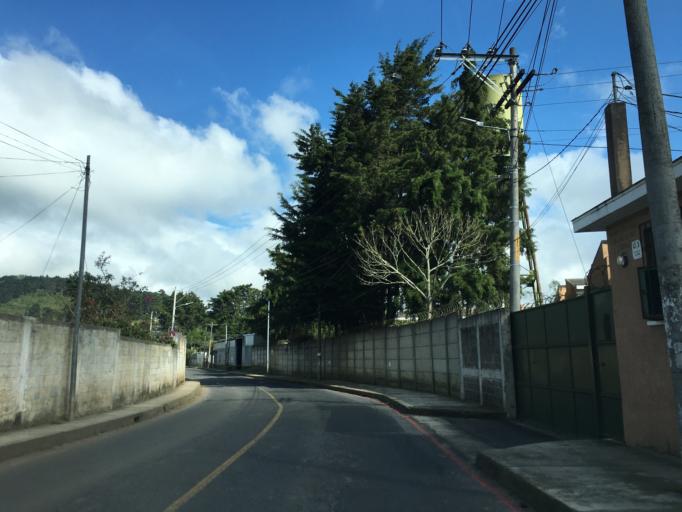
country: GT
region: Guatemala
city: San Jose Pinula
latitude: 14.5460
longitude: -90.4422
